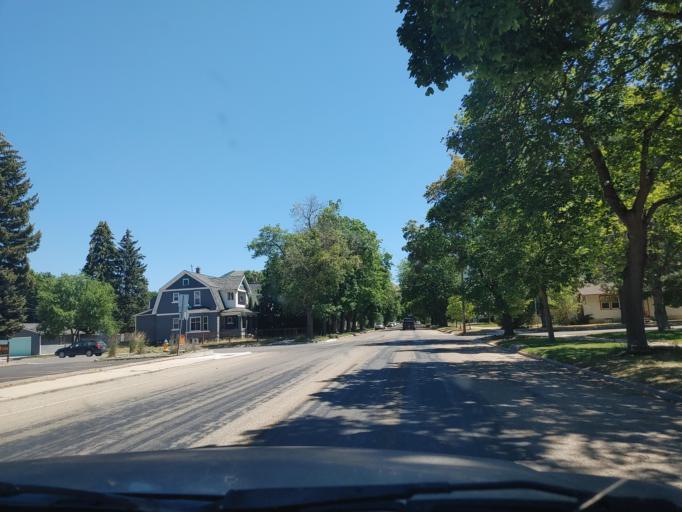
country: US
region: Montana
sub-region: Missoula County
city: Missoula
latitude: 46.8669
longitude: -114.0087
